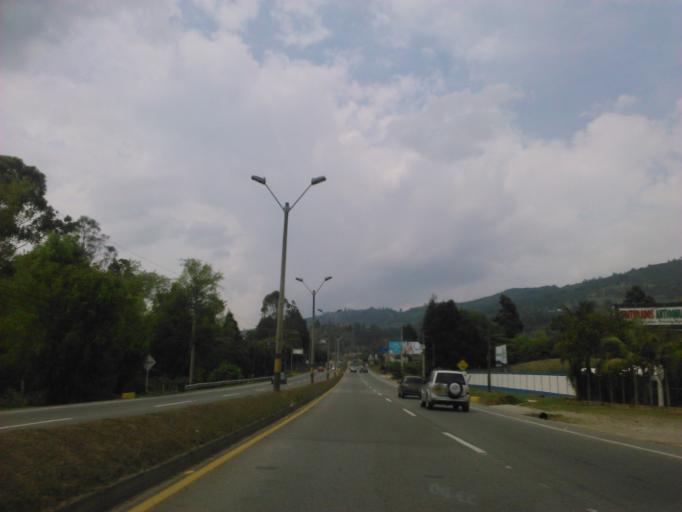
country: CO
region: Antioquia
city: Guarne
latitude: 6.2643
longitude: -75.4383
